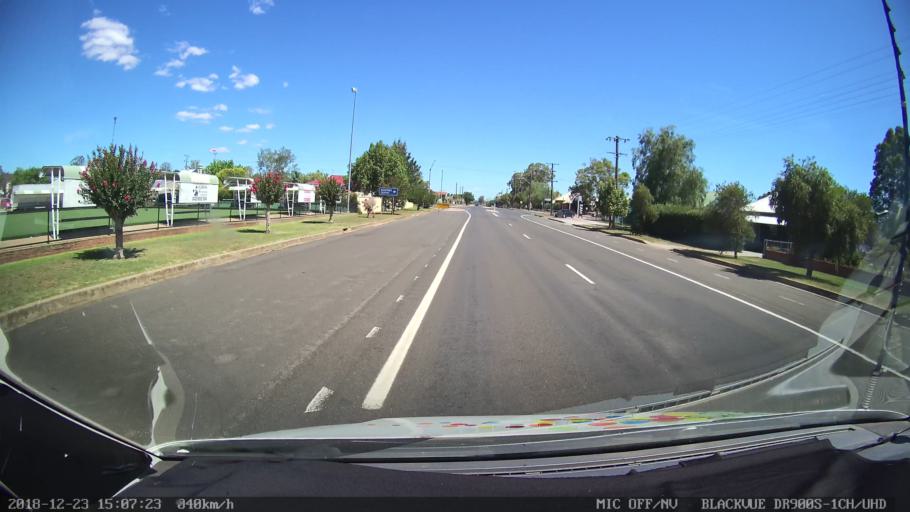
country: AU
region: New South Wales
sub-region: Tamworth Municipality
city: Manilla
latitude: -30.7476
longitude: 150.7244
